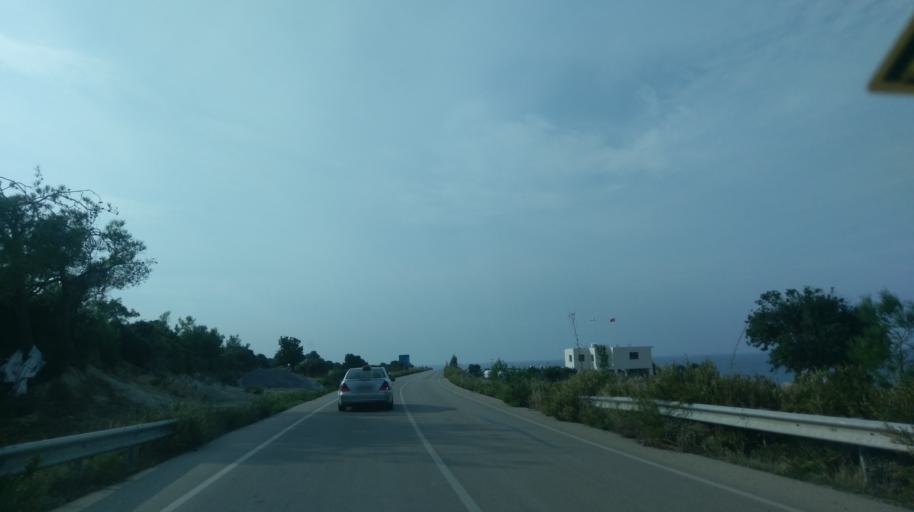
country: CY
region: Ammochostos
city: Trikomo
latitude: 35.4112
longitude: 33.8519
